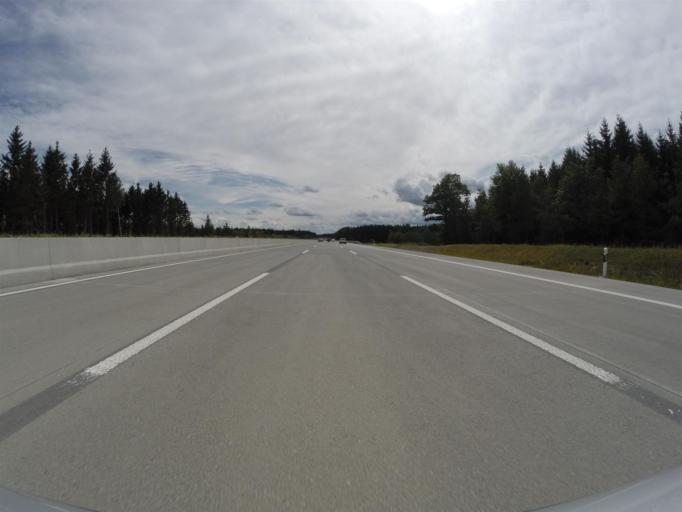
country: DE
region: Thuringia
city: Dittersdorf
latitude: 50.6388
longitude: 11.7988
